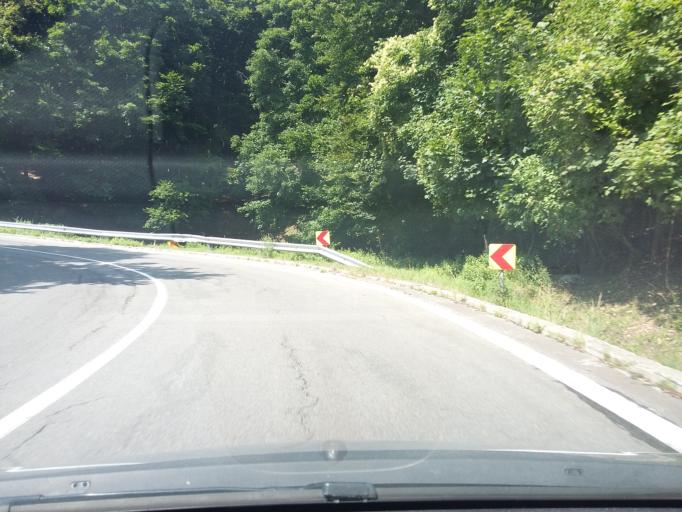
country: SK
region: Bratislavsky
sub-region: Okres Pezinok
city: Pezinok
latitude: 48.3498
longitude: 17.2096
